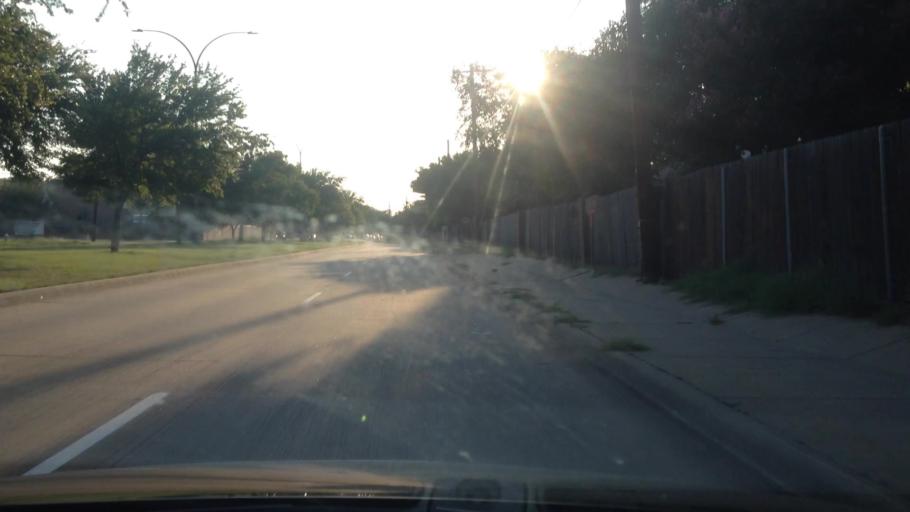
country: US
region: Texas
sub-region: Tarrant County
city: Dalworthington Gardens
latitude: 32.6488
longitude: -97.1384
